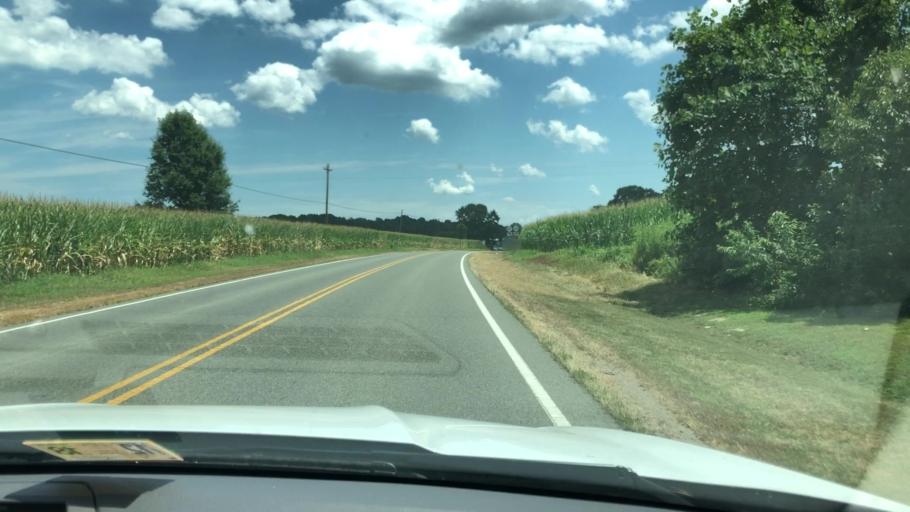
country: US
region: Virginia
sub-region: Lancaster County
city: Lancaster
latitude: 37.7973
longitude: -76.5239
